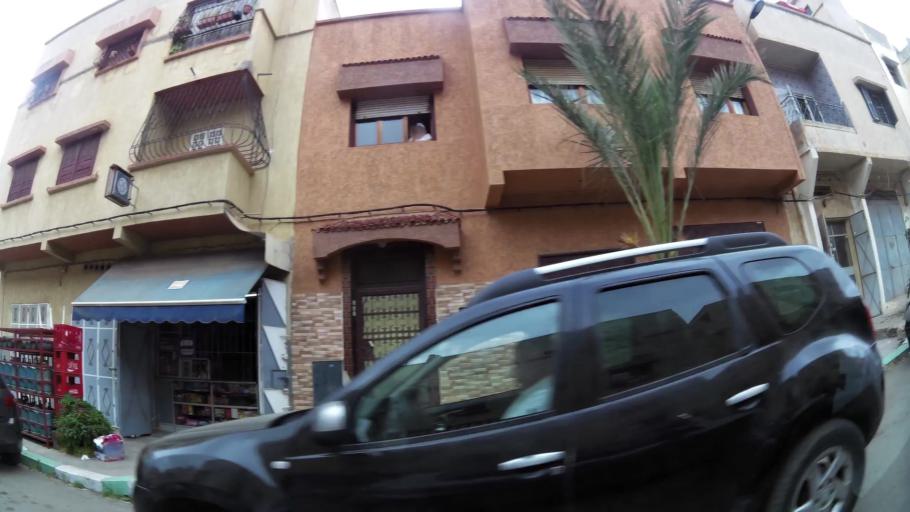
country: MA
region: Rabat-Sale-Zemmour-Zaer
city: Sale
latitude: 34.0403
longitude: -6.8054
